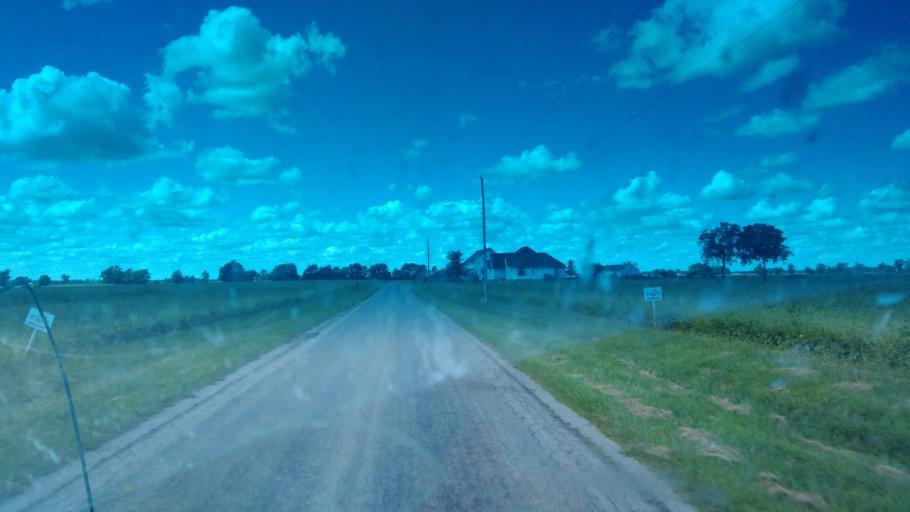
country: US
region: Ohio
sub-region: Madison County
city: Plain City
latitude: 40.0773
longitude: -83.3490
